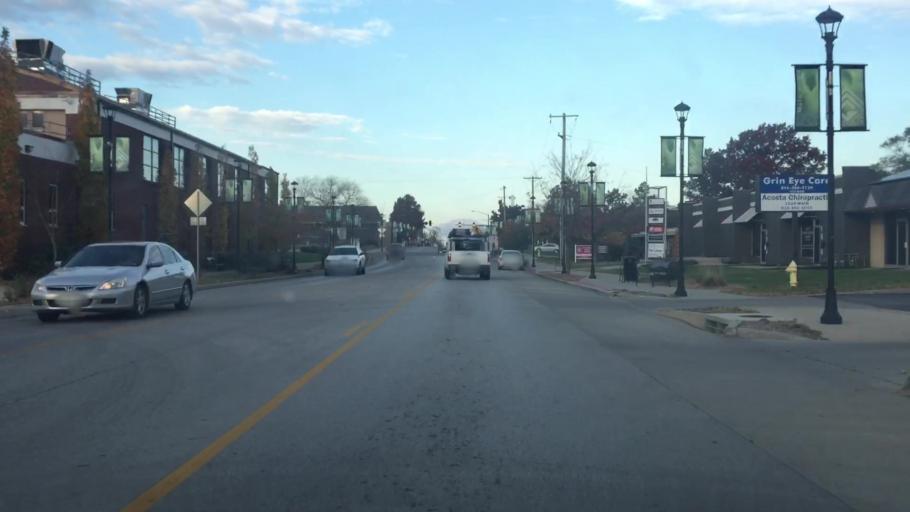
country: US
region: Missouri
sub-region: Jackson County
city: Grandview
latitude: 38.8893
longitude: -94.5323
